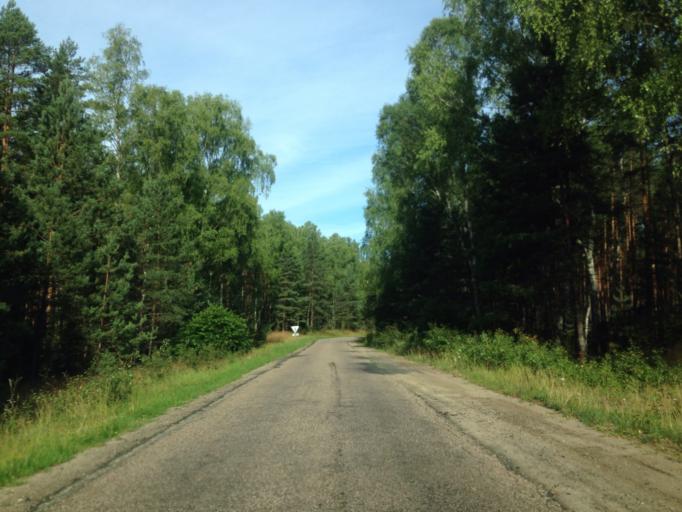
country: PL
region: Kujawsko-Pomorskie
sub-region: Powiat swiecki
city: Osie
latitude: 53.6970
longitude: 18.3701
